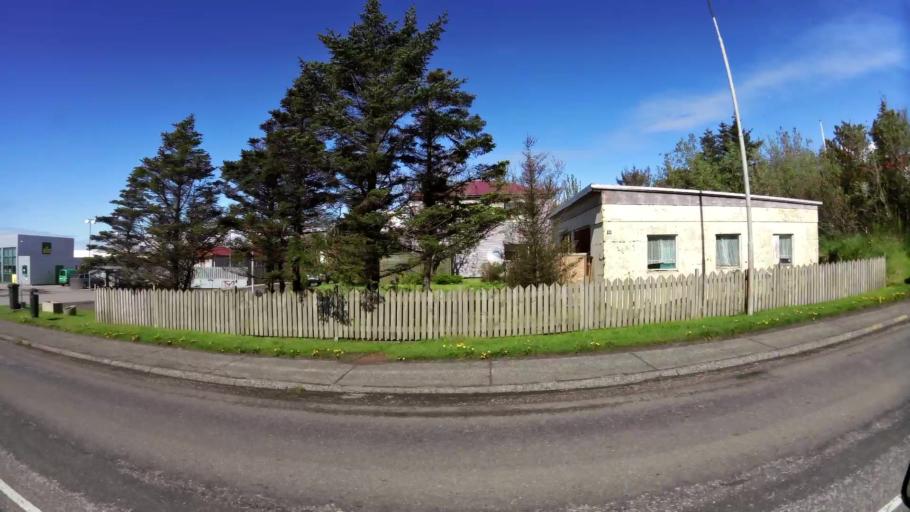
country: IS
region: East
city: Hoefn
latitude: 64.2558
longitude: -15.2078
